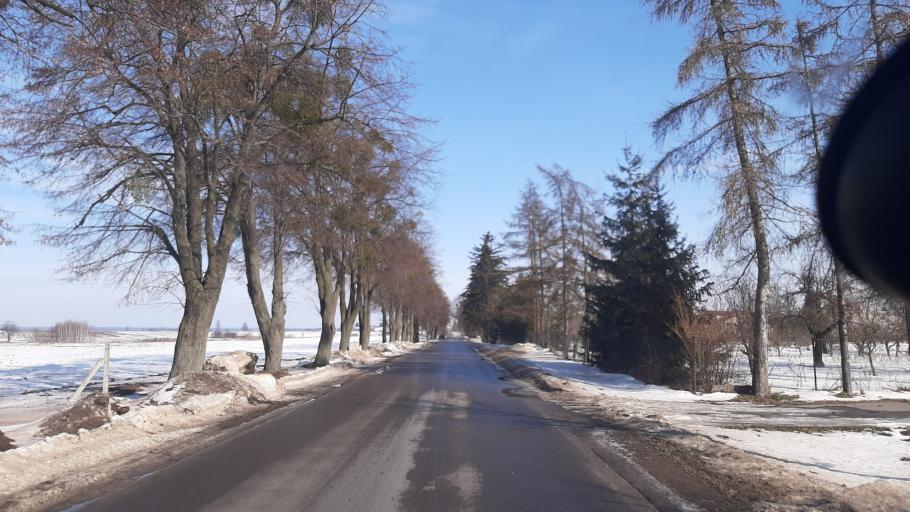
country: PL
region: Lublin Voivodeship
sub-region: Powiat pulawski
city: Kurow
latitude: 51.3796
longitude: 22.1585
